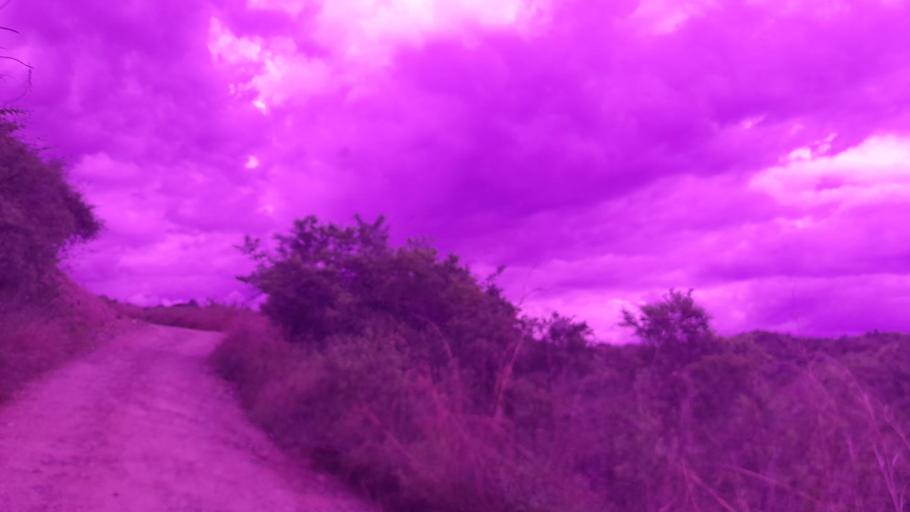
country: CO
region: Valle del Cauca
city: Andalucia
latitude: 4.1724
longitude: -76.1244
